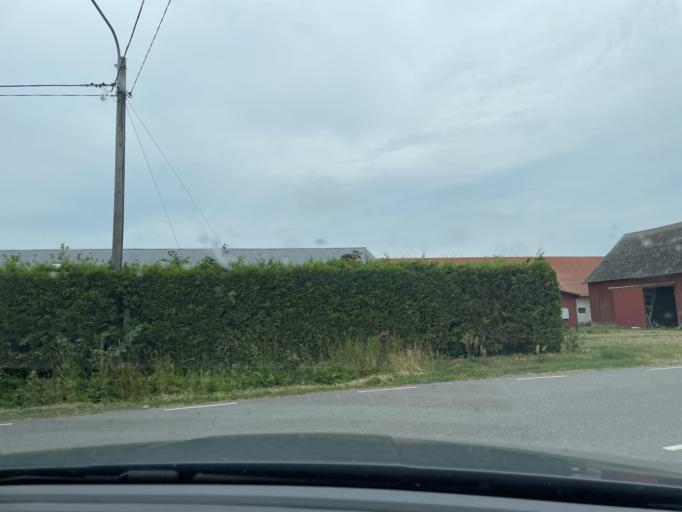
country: SE
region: Skane
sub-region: Bromolla Kommun
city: Bromoella
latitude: 56.0105
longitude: 14.4350
